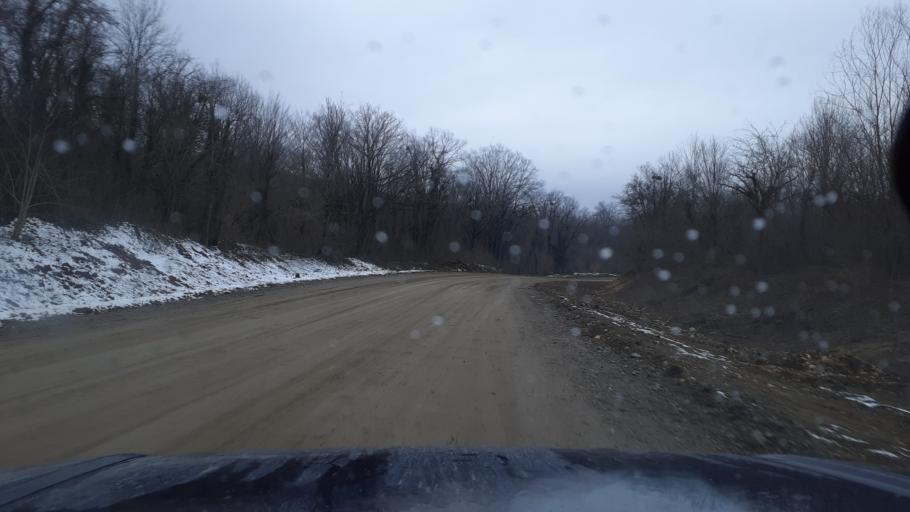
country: RU
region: Krasnodarskiy
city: Neftegorsk
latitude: 44.2080
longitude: 39.8179
